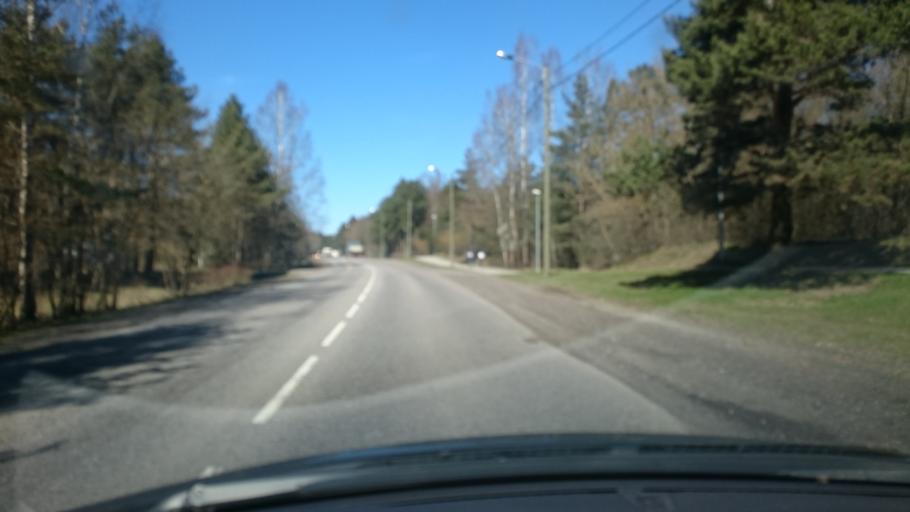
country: EE
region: Harju
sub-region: Tallinna linn
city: Kose
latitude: 59.4704
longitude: 24.9019
